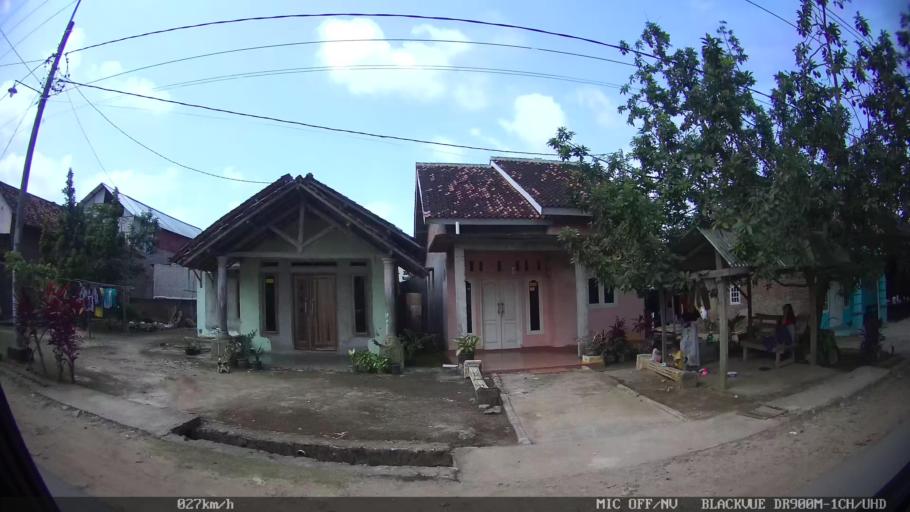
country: ID
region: Lampung
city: Kedaton
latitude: -5.3412
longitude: 105.2826
